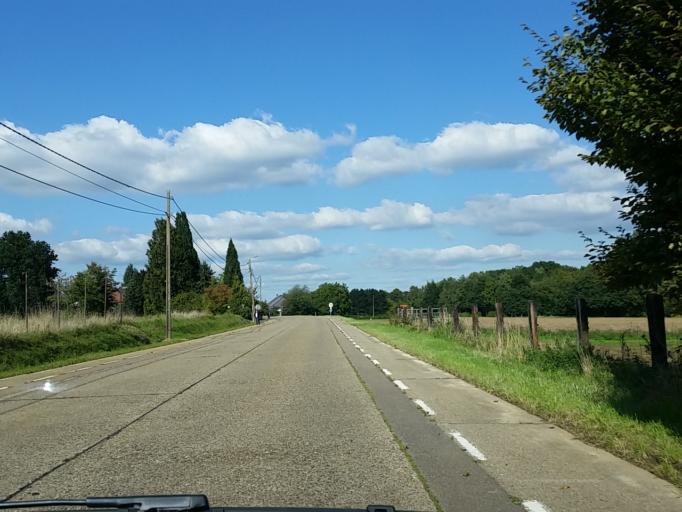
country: BE
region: Flanders
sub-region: Provincie Vlaams-Brabant
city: Lubbeek
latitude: 50.9129
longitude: 4.8417
